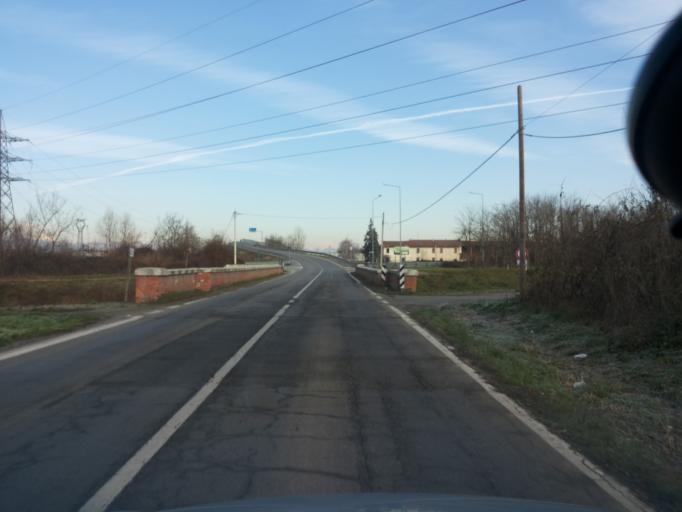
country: IT
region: Piedmont
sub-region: Provincia di Vercelli
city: Greggio
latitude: 45.4579
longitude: 8.3855
